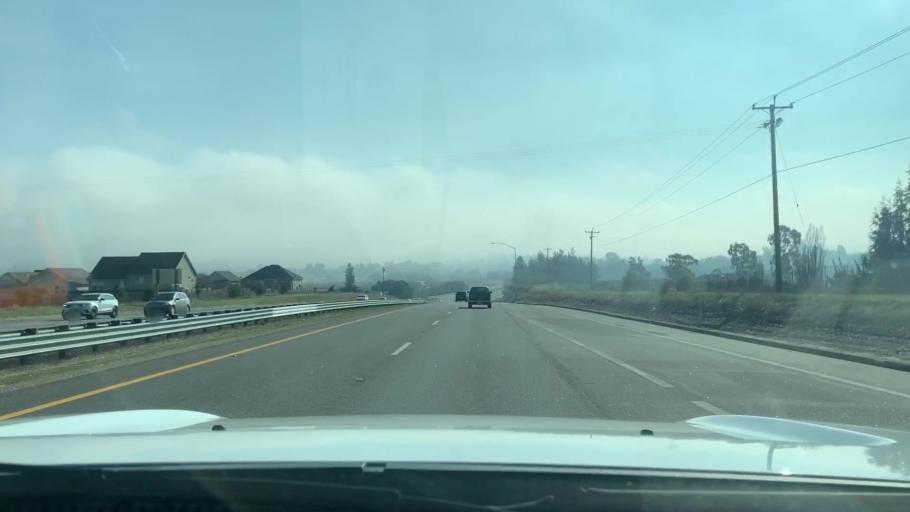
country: US
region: California
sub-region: San Luis Obispo County
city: Atascadero
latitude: 35.4564
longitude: -120.6440
